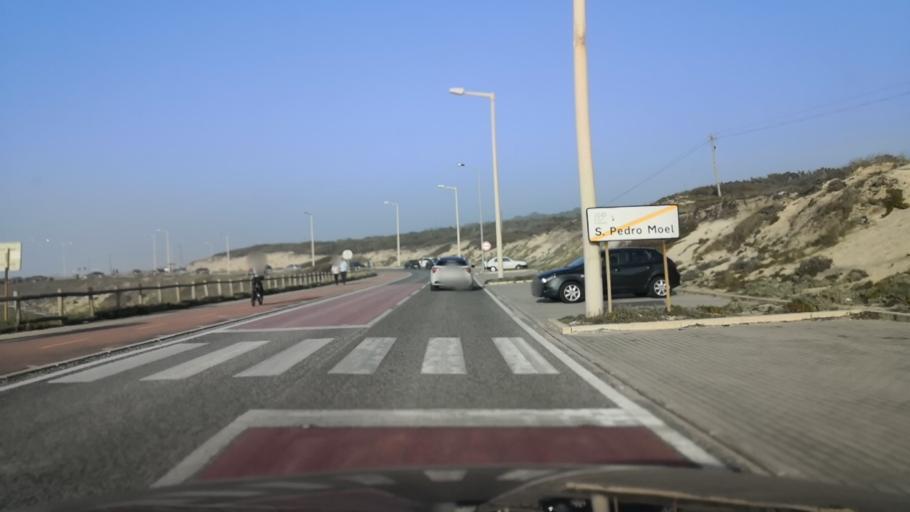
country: PT
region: Leiria
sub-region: Marinha Grande
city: Marinha Grande
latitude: 39.7671
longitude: -9.0293
